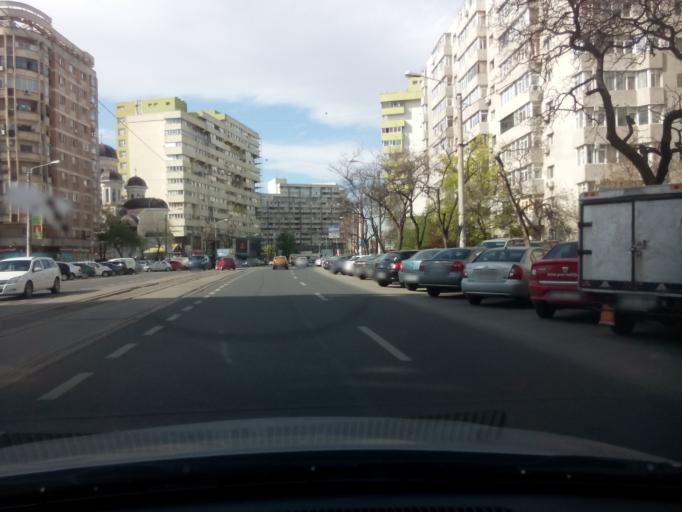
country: RO
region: Ilfov
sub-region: Comuna Fundeni-Dobroesti
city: Fundeni
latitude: 44.4407
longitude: 26.1577
